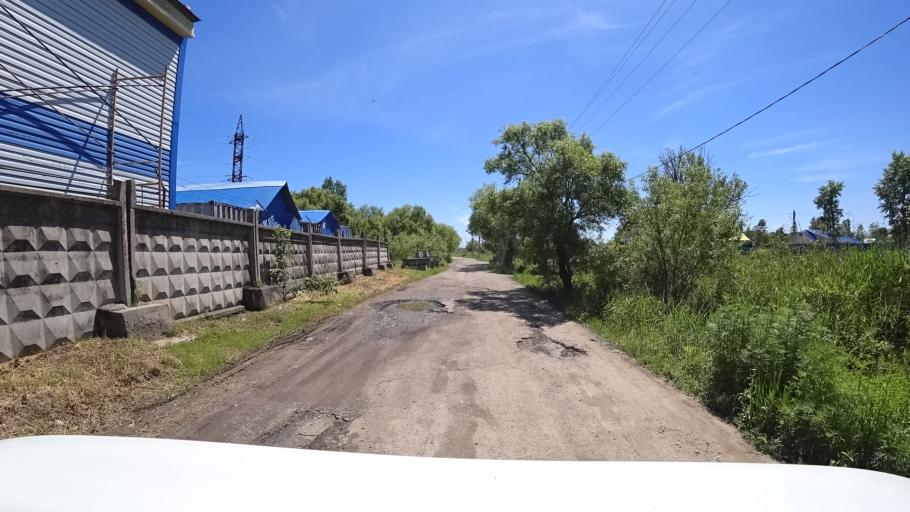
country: RU
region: Khabarovsk Krai
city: Topolevo
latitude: 48.5001
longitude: 135.1826
